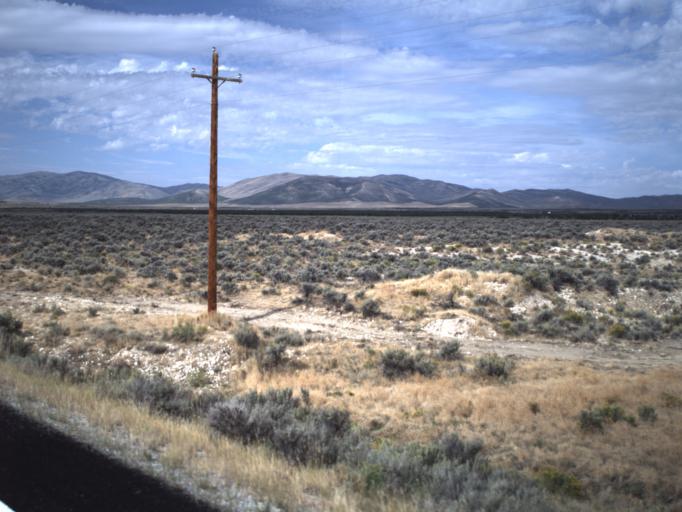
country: US
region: Idaho
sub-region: Cassia County
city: Burley
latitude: 41.7945
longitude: -113.4665
